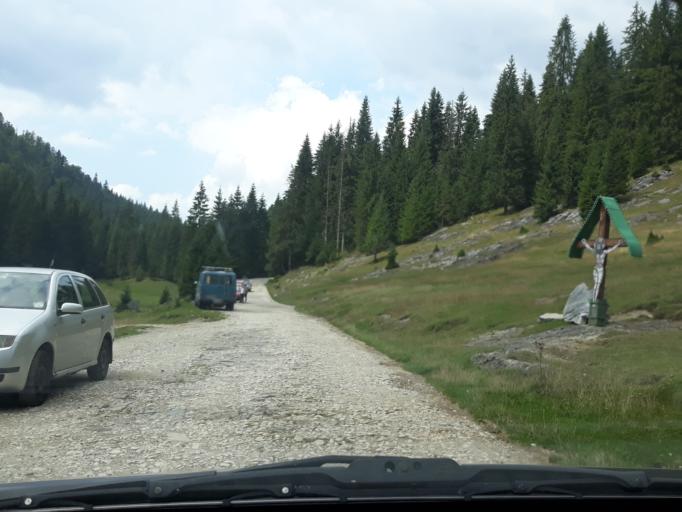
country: RO
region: Alba
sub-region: Comuna Arieseni
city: Arieseni
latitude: 46.5796
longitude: 22.7034
